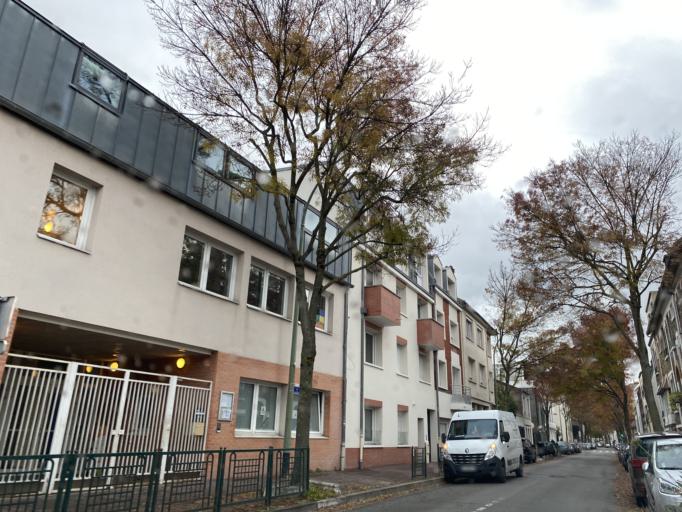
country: FR
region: Ile-de-France
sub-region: Departement des Hauts-de-Seine
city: Suresnes
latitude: 48.8640
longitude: 2.2230
